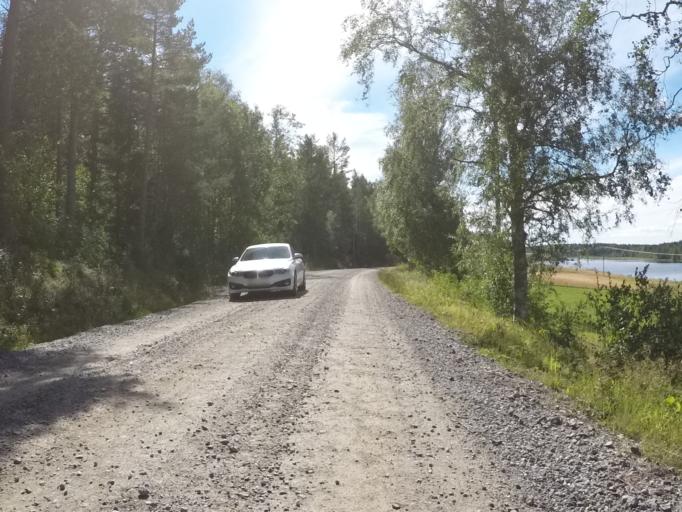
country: SE
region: Vaesterbotten
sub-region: Robertsfors Kommun
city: Robertsfors
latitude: 64.0090
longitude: 20.8174
